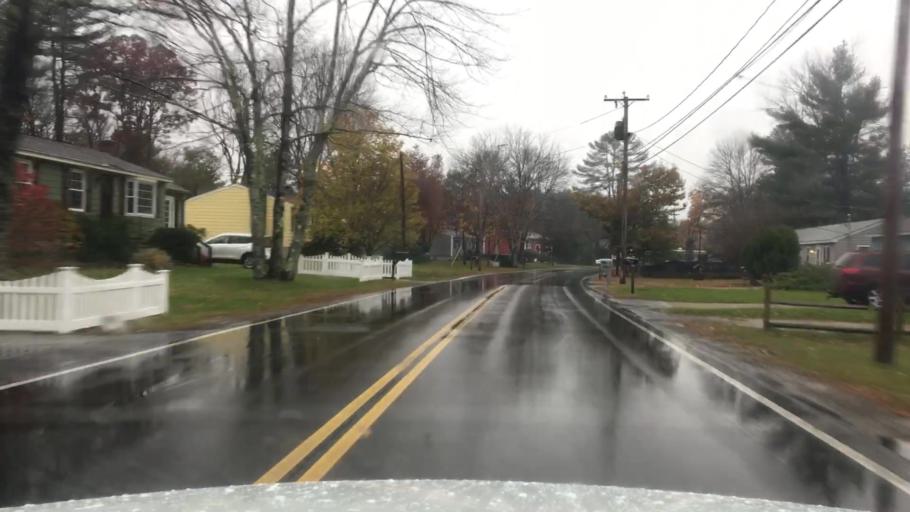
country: US
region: New Hampshire
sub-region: Strafford County
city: Rochester
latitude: 43.3426
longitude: -70.9686
